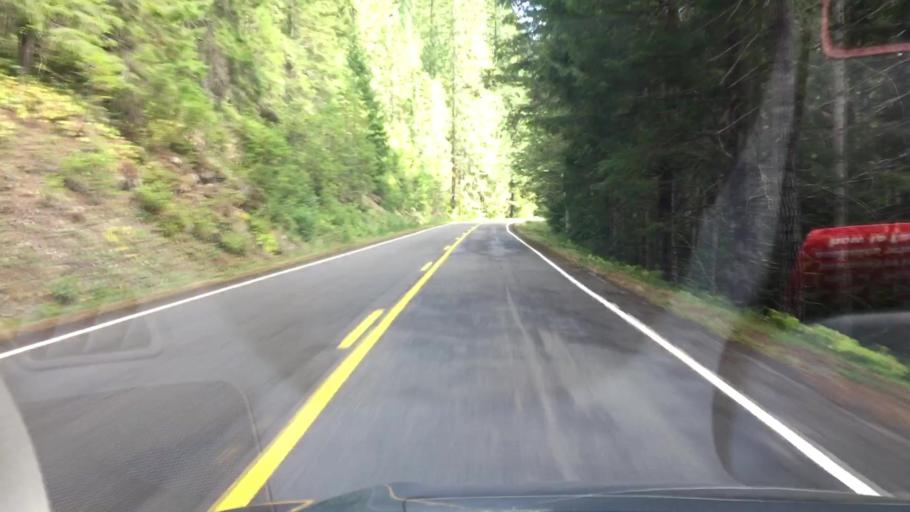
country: US
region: Washington
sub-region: Pierce County
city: Buckley
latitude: 46.7479
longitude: -121.6197
